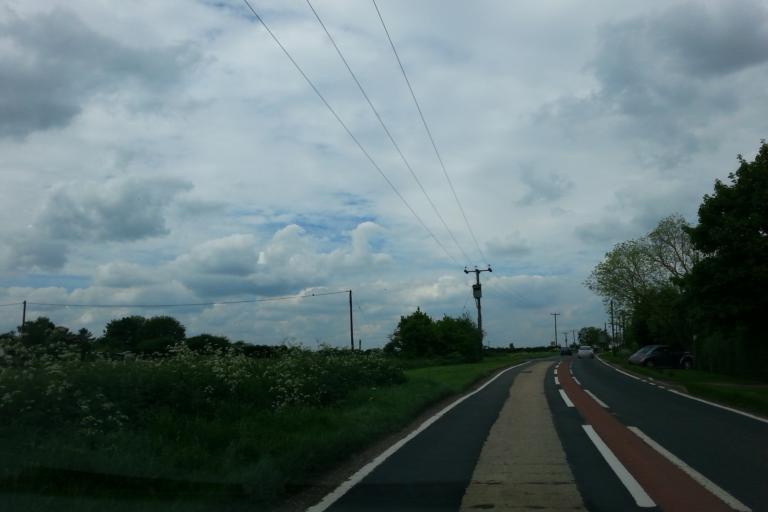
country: GB
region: England
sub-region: Cambridgeshire
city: Warboys
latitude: 52.4154
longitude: -0.1065
